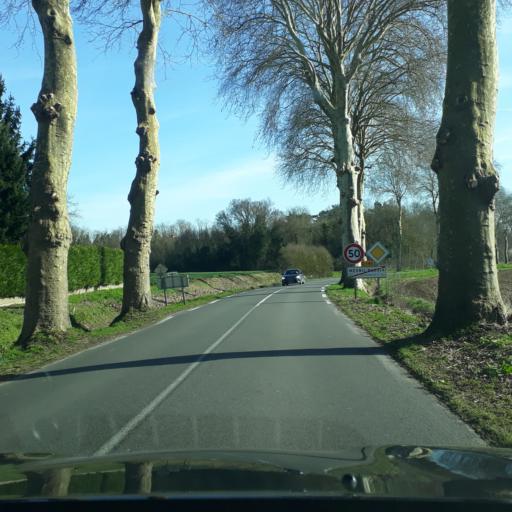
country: FR
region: Ile-de-France
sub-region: Departement de l'Essonne
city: Boissy-le-Cutte
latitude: 48.4574
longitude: 2.2613
